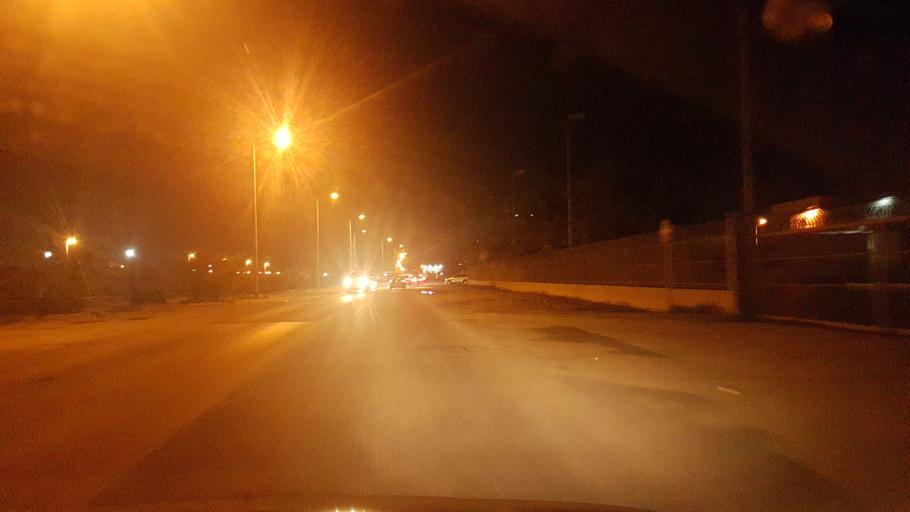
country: BH
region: Muharraq
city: Al Hadd
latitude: 26.2753
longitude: 50.6404
